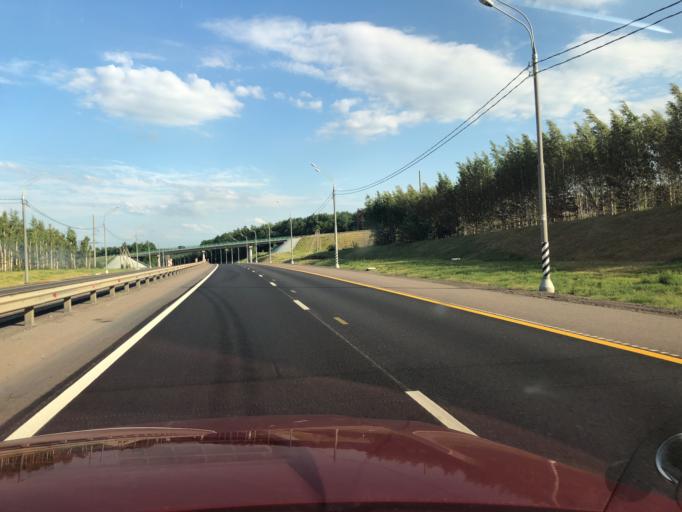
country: RU
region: Lipetsk
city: Zadonsk
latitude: 52.3879
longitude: 38.8665
